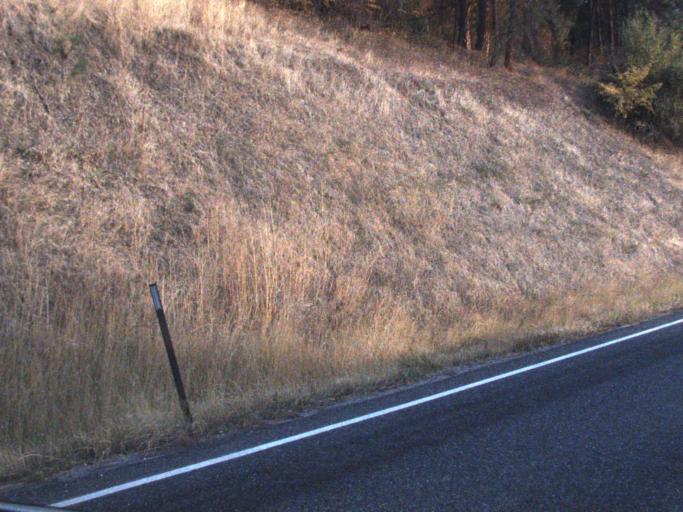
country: US
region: Washington
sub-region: Stevens County
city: Kettle Falls
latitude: 48.6958
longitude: -118.0133
